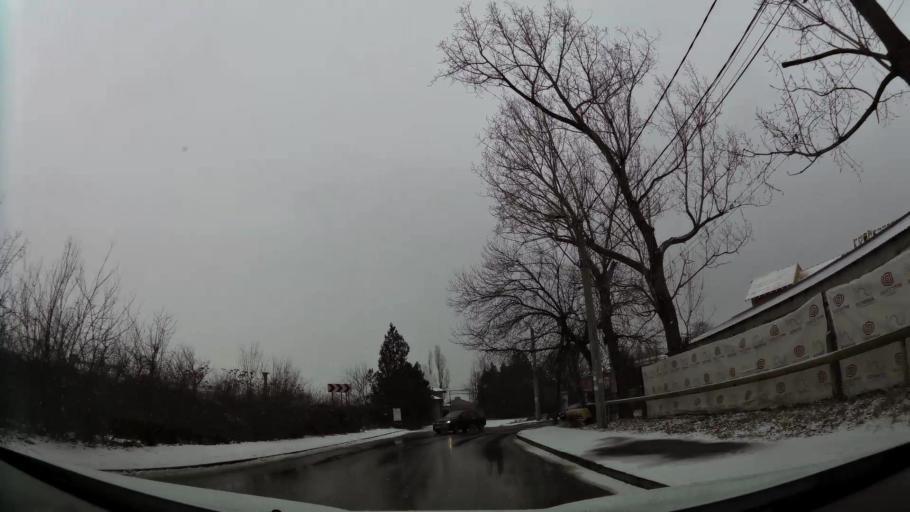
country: RO
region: Prahova
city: Ploiesti
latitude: 44.9220
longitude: 26.0081
